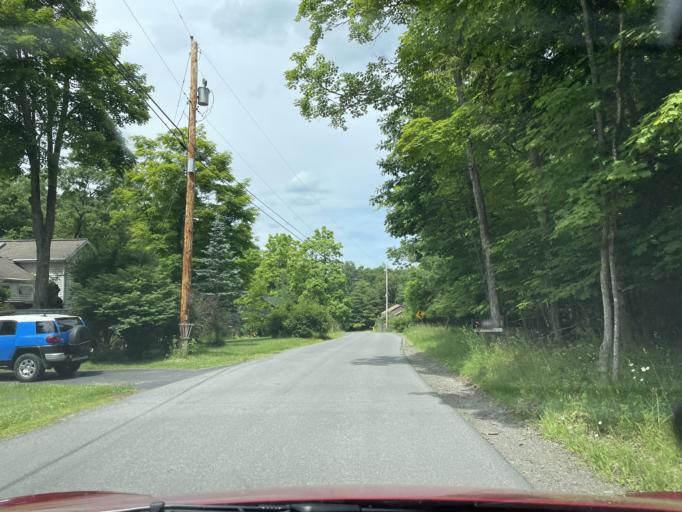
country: US
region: New York
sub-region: Ulster County
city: Zena
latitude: 41.9870
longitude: -74.0615
